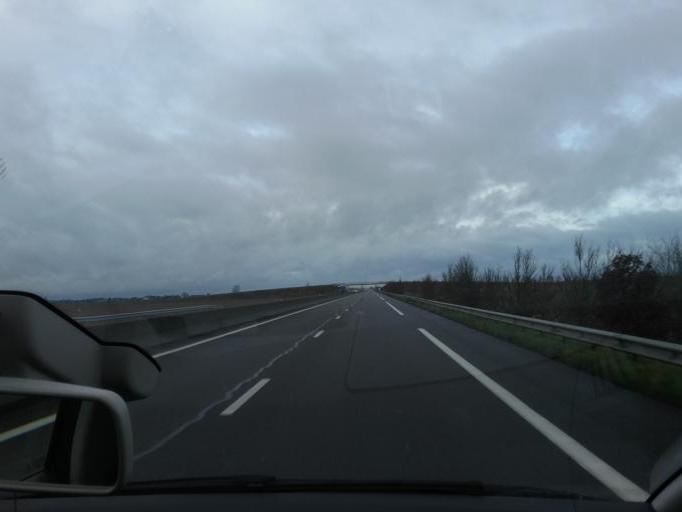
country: FR
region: Picardie
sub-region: Departement de la Somme
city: Harbonnieres
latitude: 49.8550
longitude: 2.6184
